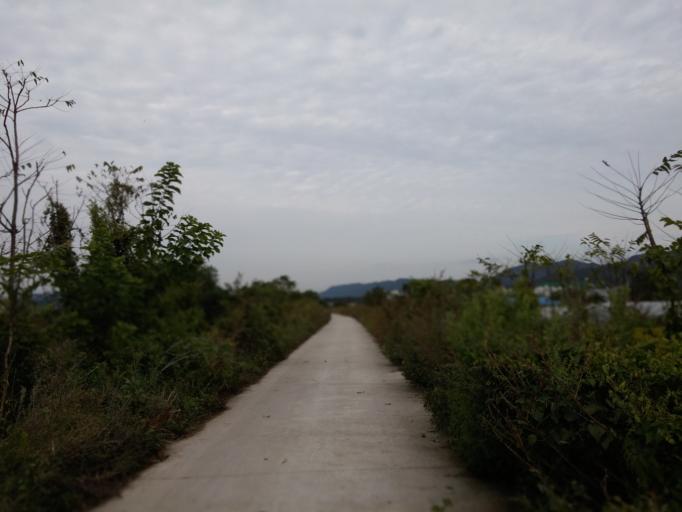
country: KR
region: Chungcheongnam-do
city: Yonmu
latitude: 36.1680
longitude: 127.2022
